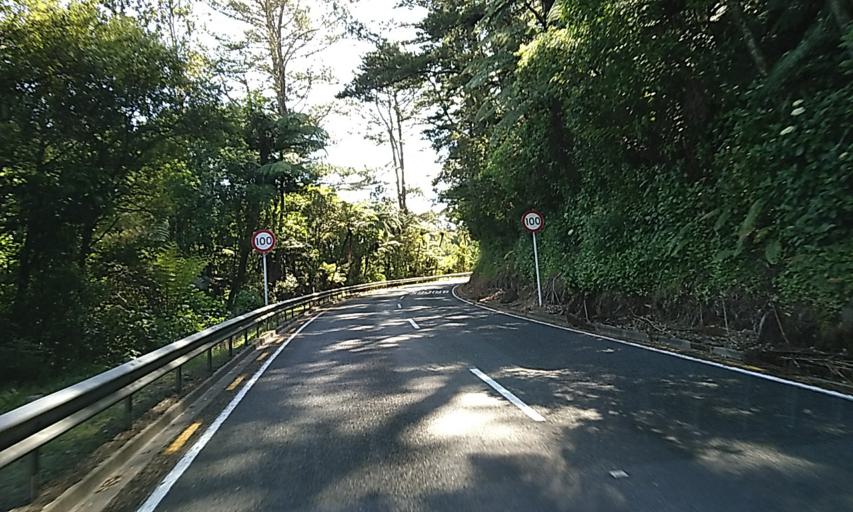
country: NZ
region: Bay of Plenty
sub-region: Tauranga City
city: Tauranga
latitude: -37.8053
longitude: 176.0443
